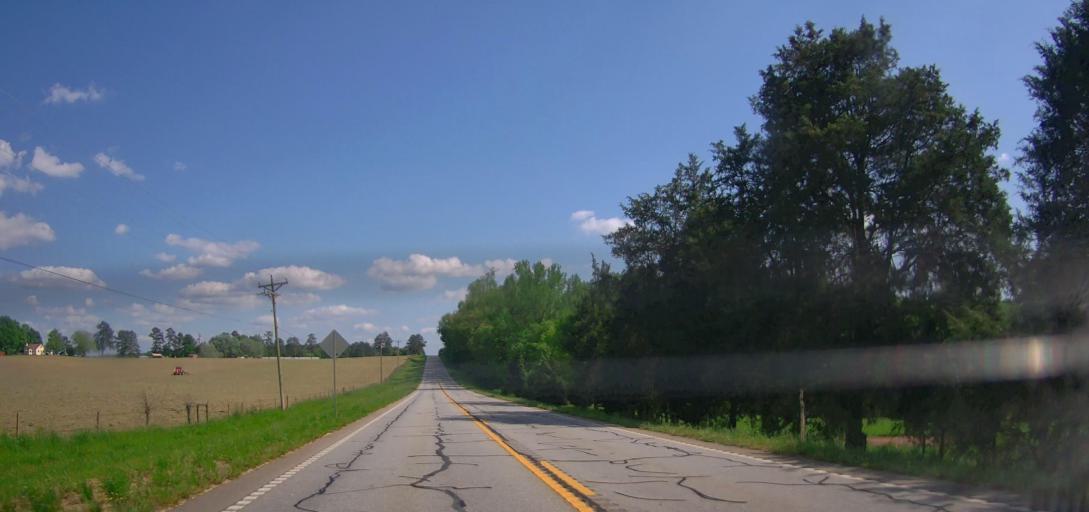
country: US
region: Georgia
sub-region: Greene County
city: Greensboro
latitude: 33.6094
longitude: -83.3111
